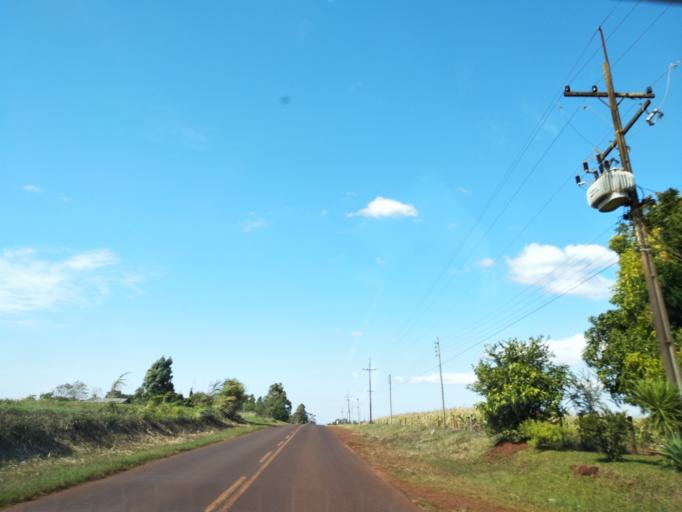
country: PY
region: Itapua
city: Hohenau
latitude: -27.0648
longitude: -55.7262
